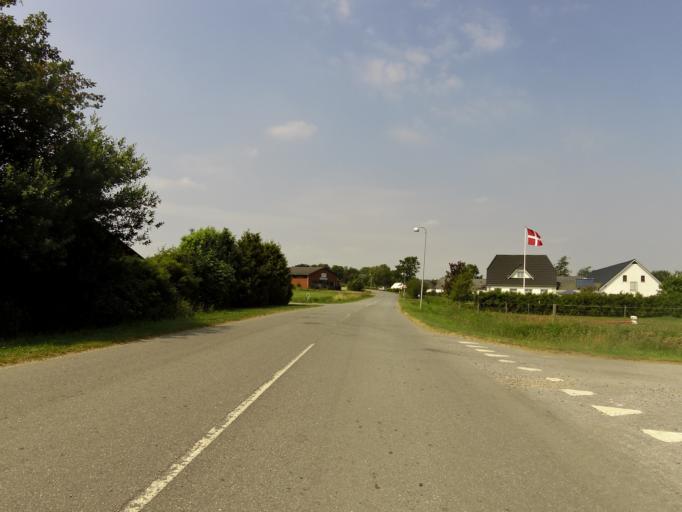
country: DK
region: South Denmark
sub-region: Aabenraa Kommune
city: Rodekro
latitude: 55.1413
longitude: 9.2083
